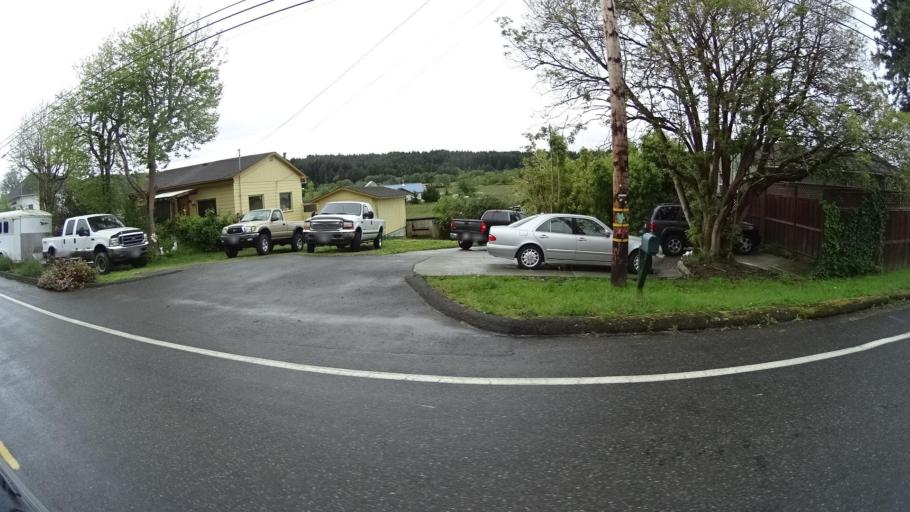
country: US
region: California
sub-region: Humboldt County
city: Bayside
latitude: 40.8412
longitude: -124.0612
